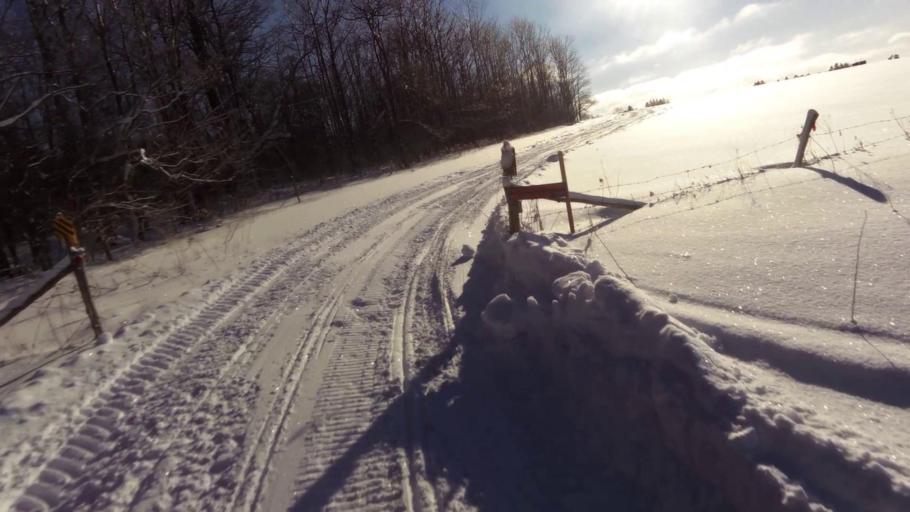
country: US
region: New York
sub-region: Chautauqua County
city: Falconer
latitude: 42.2696
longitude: -79.2004
